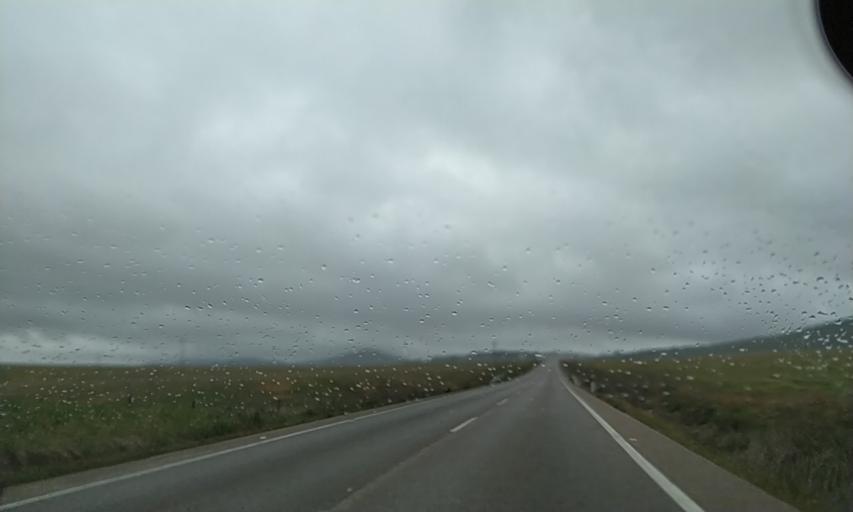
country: ES
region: Extremadura
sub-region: Provincia de Caceres
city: Caceres
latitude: 39.5048
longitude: -6.3907
